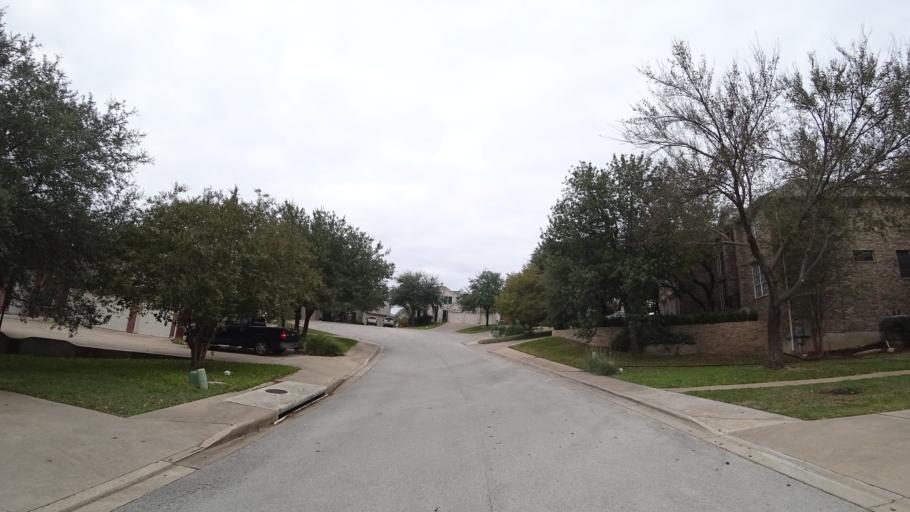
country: US
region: Texas
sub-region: Travis County
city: Bee Cave
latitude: 30.3170
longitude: -97.9180
